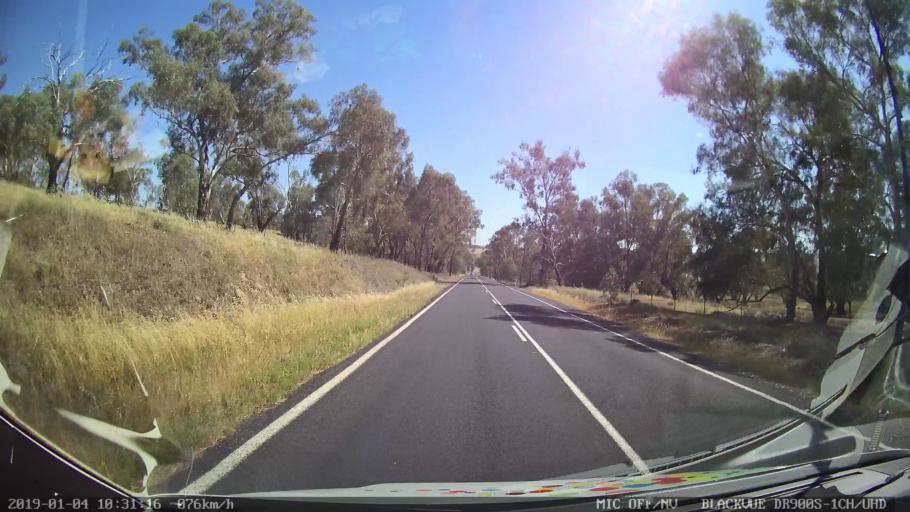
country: AU
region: New South Wales
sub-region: Cabonne
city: Canowindra
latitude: -33.3367
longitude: 148.6319
